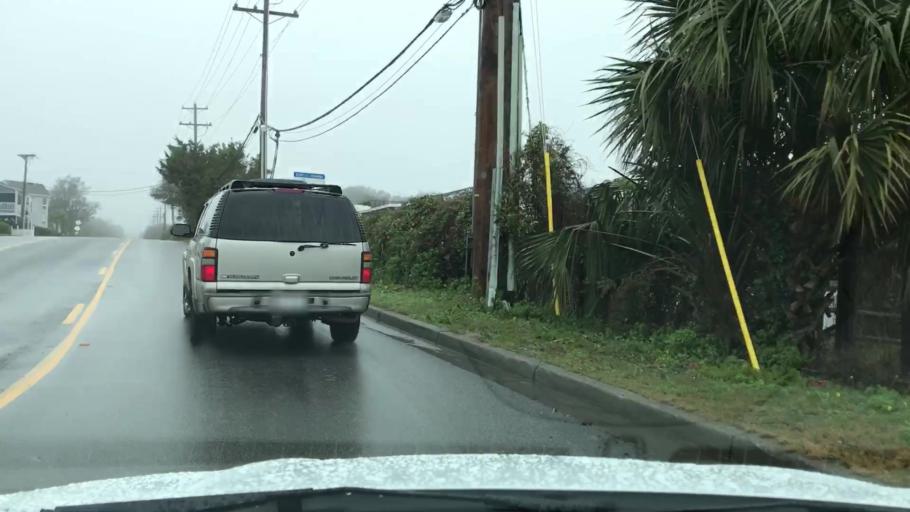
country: US
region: South Carolina
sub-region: Horry County
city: North Myrtle Beach
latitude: 33.7636
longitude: -78.7850
